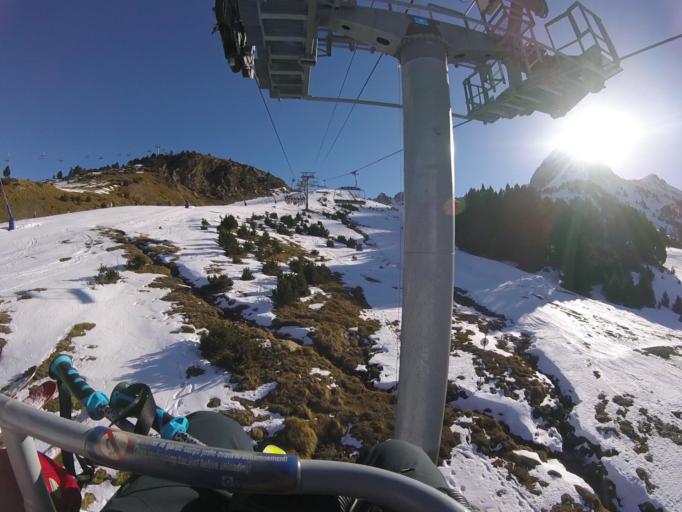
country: AD
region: Encamp
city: Pas de la Casa
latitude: 42.5287
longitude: 1.7018
